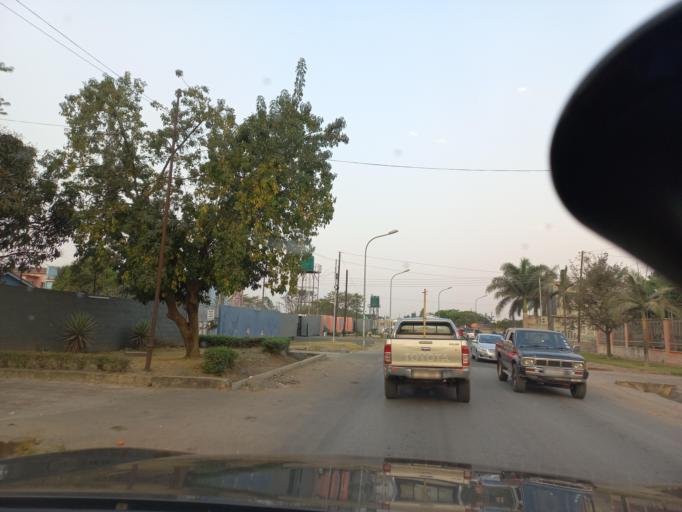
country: ZM
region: Lusaka
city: Lusaka
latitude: -15.4046
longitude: 28.2801
